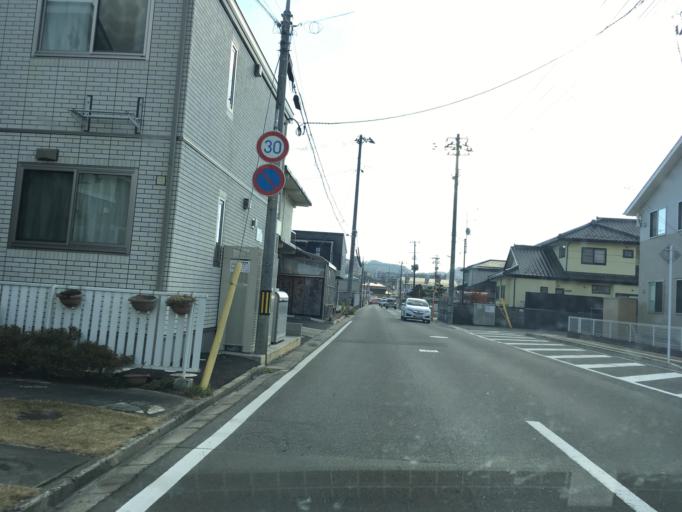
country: JP
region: Miyagi
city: Sendai
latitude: 38.2725
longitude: 140.7645
